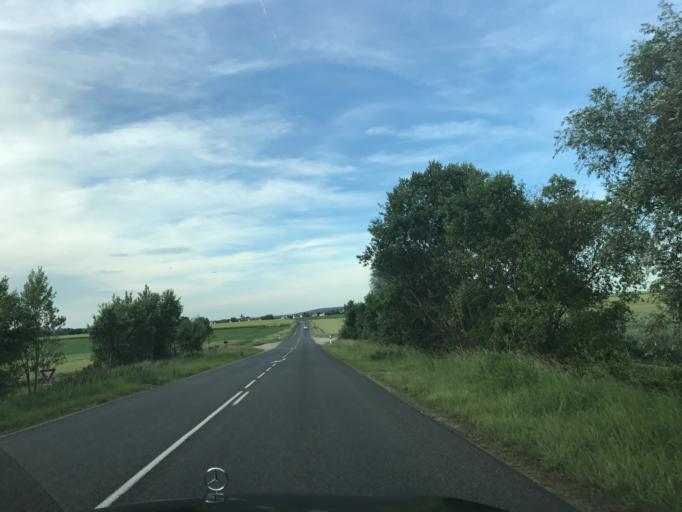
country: FR
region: Ile-de-France
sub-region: Departement de Seine-et-Marne
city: Claye-Souilly
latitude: 48.9563
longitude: 2.6962
